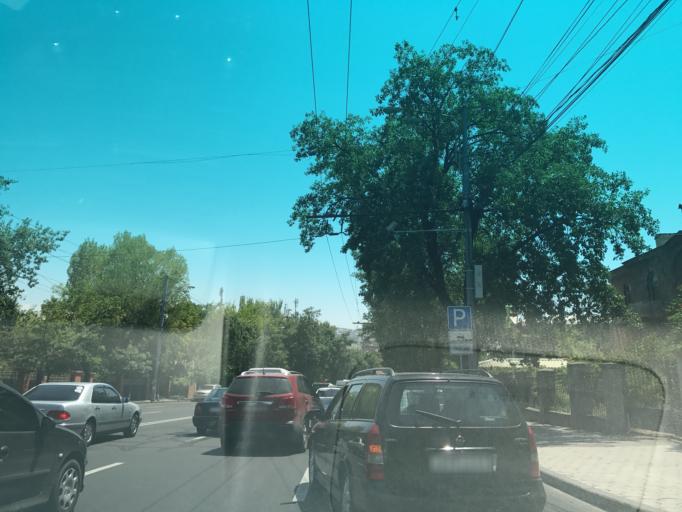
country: AM
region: Yerevan
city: Yerevan
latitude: 40.1911
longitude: 44.5111
